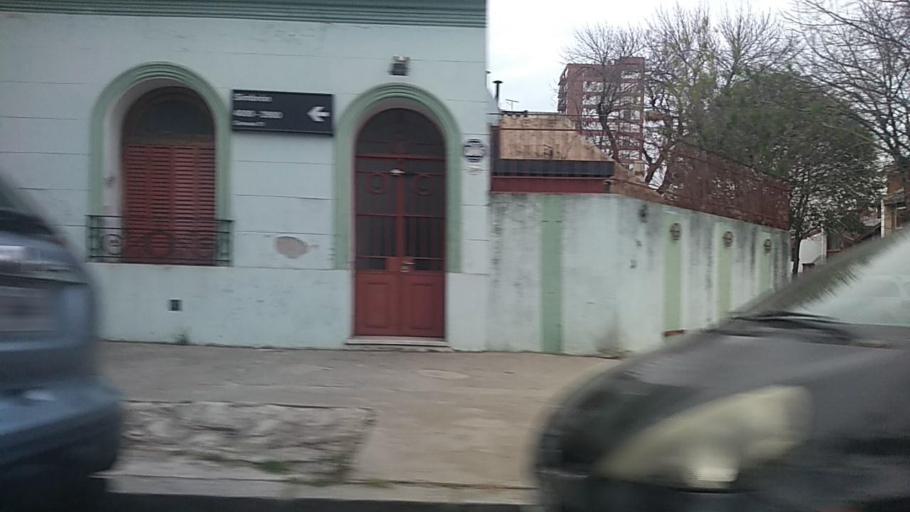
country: AR
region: Buenos Aires F.D.
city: Villa Santa Rita
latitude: -34.6049
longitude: -58.5061
